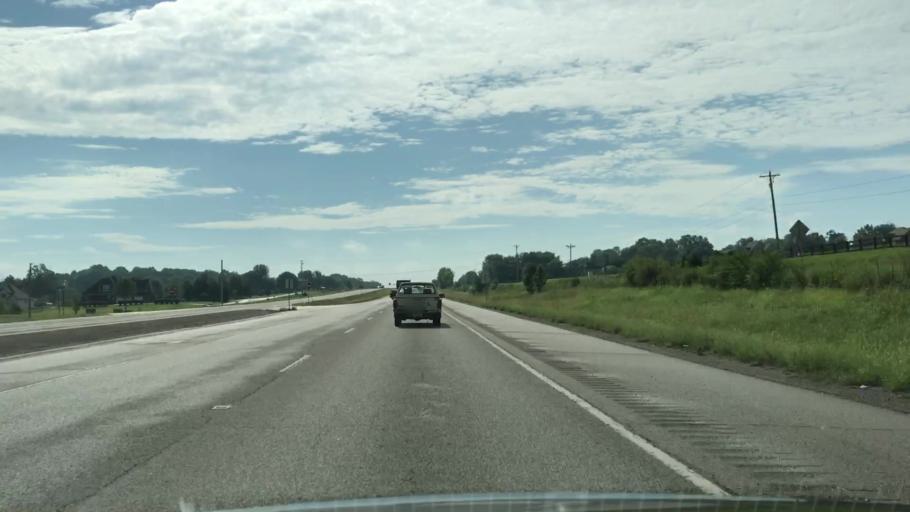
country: US
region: Kentucky
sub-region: Warren County
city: Plano
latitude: 36.8944
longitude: -86.3788
